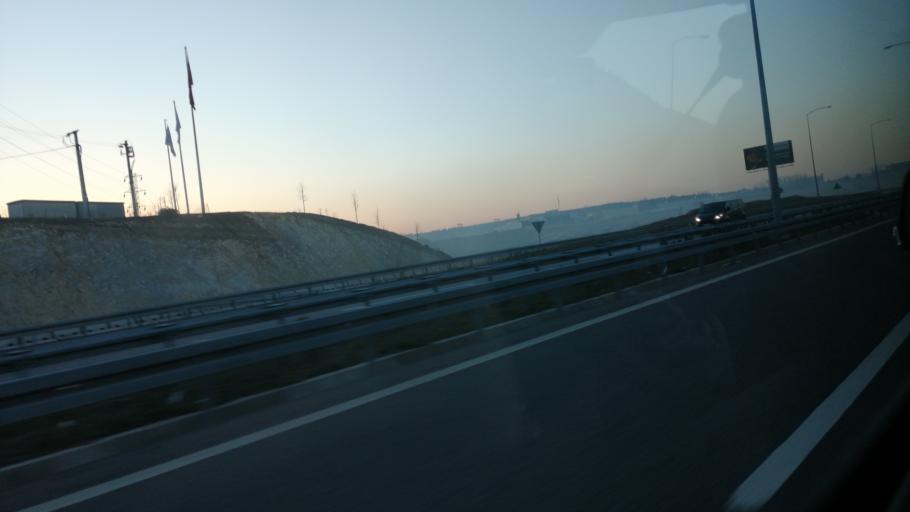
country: TR
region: Kocaeli
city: Tavsanli
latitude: 40.7932
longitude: 29.5120
